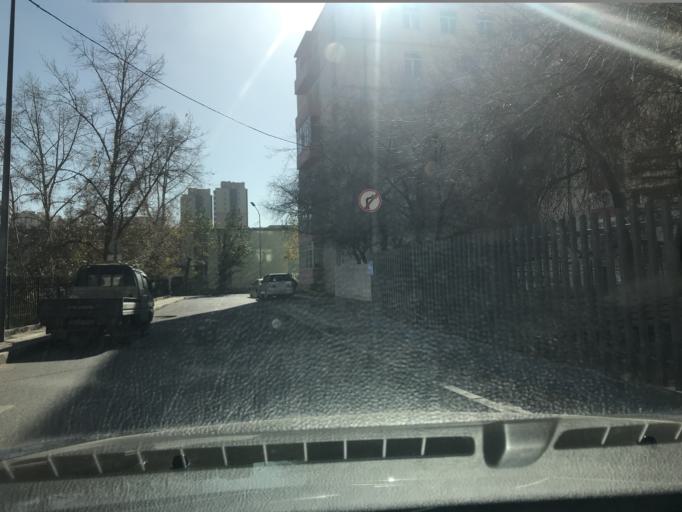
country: MN
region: Ulaanbaatar
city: Ulaanbaatar
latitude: 47.9181
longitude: 106.9029
